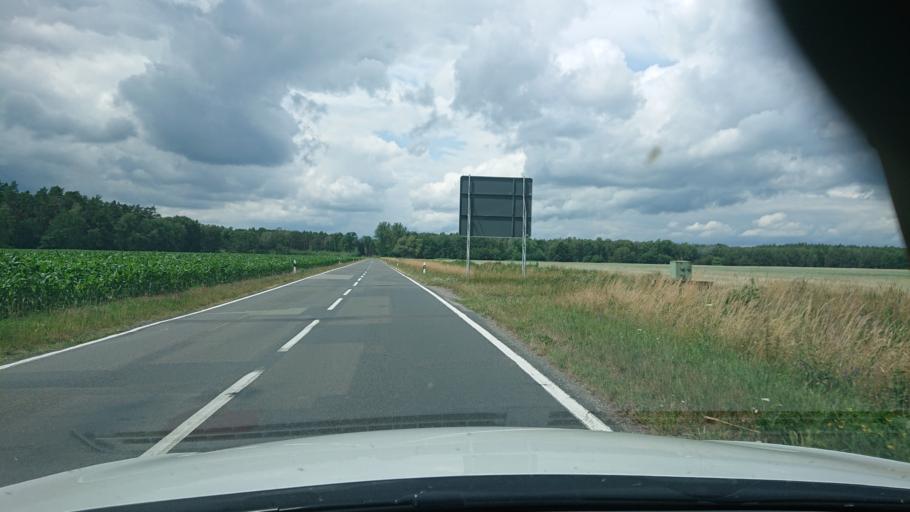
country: DE
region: Mecklenburg-Vorpommern
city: Ludwigslust
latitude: 53.3587
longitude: 11.4866
